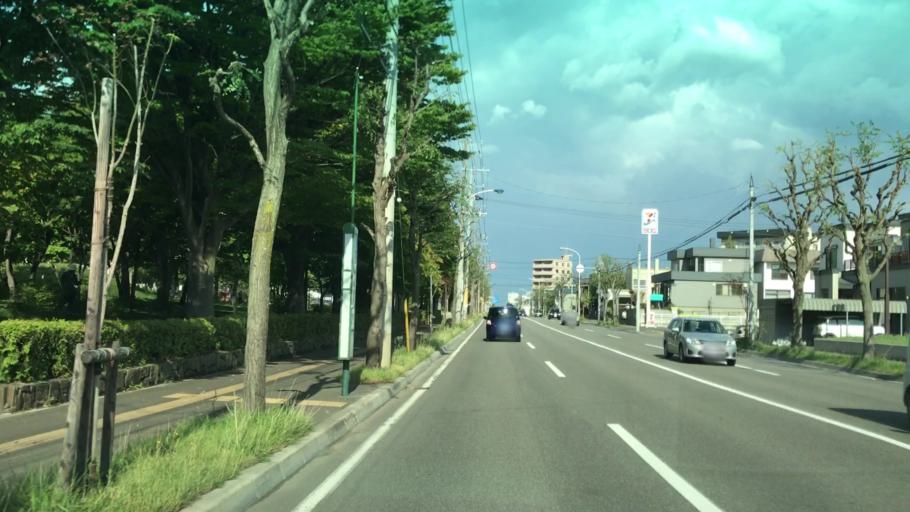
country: JP
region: Hokkaido
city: Sapporo
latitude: 43.0846
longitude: 141.2986
